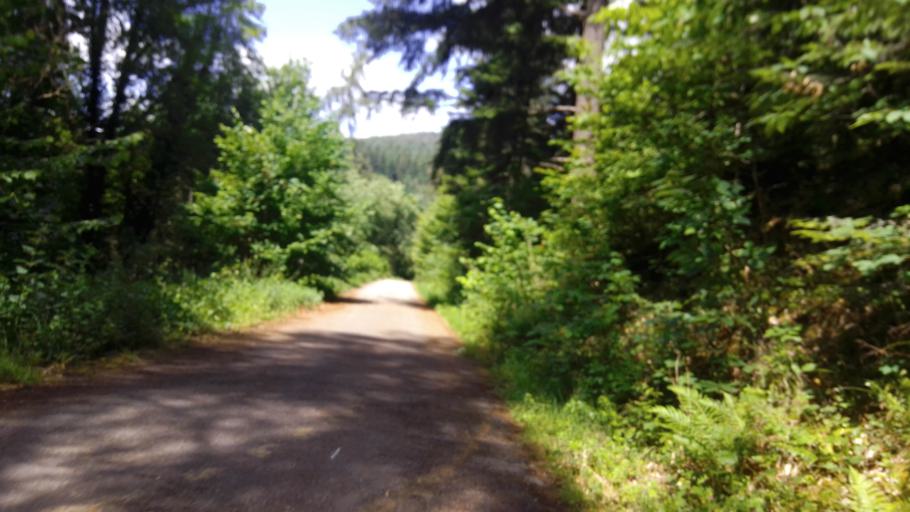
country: DE
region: Baden-Wuerttemberg
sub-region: Karlsruhe Region
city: Sinzheim
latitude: 48.7383
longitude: 8.1952
